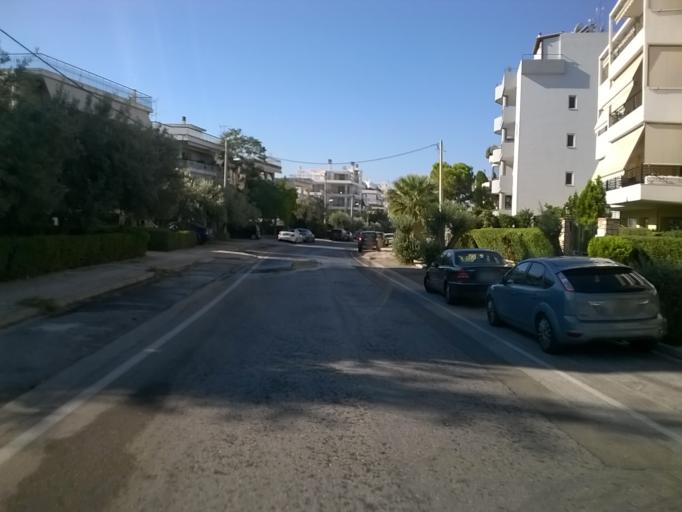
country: GR
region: Attica
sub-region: Nomarchia Athinas
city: Glyfada
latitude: 37.8667
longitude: 23.7522
